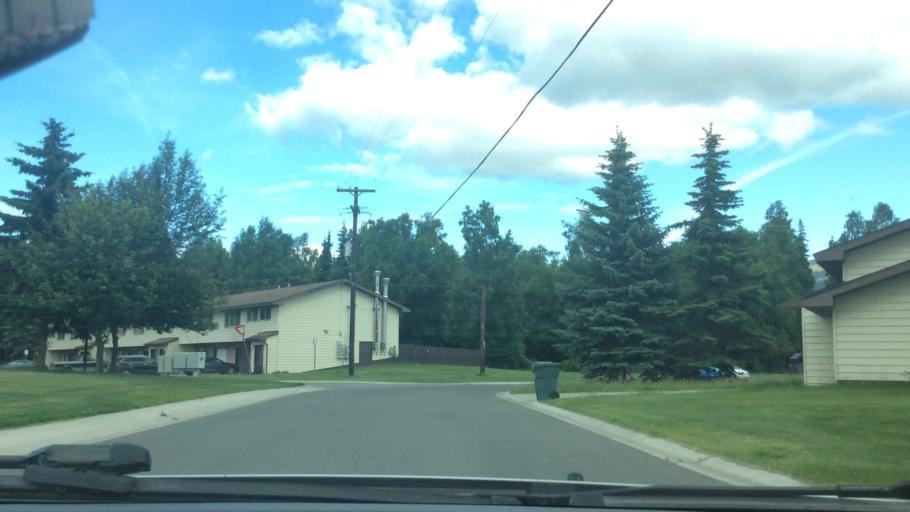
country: US
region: Alaska
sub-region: Anchorage Municipality
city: Elmendorf Air Force Base
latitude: 61.2298
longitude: -149.7537
